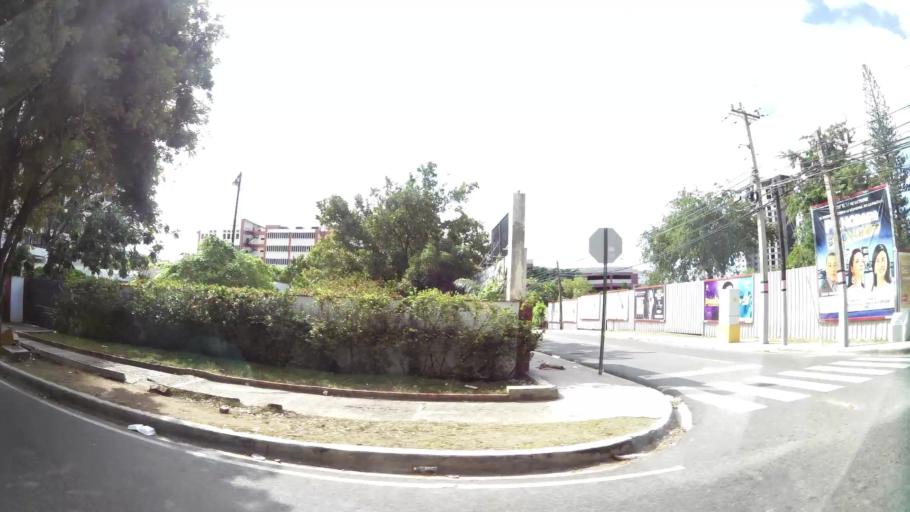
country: DO
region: Nacional
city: La Julia
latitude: 18.4609
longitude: -69.9327
